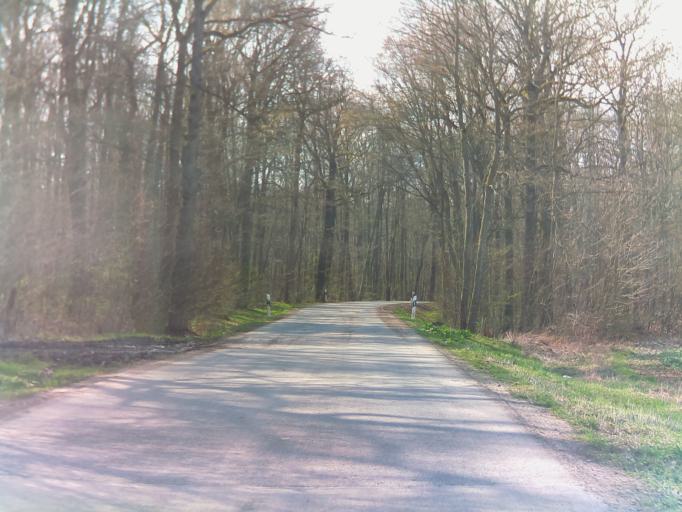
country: DE
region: Thuringia
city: Milda
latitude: 50.8514
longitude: 11.4757
